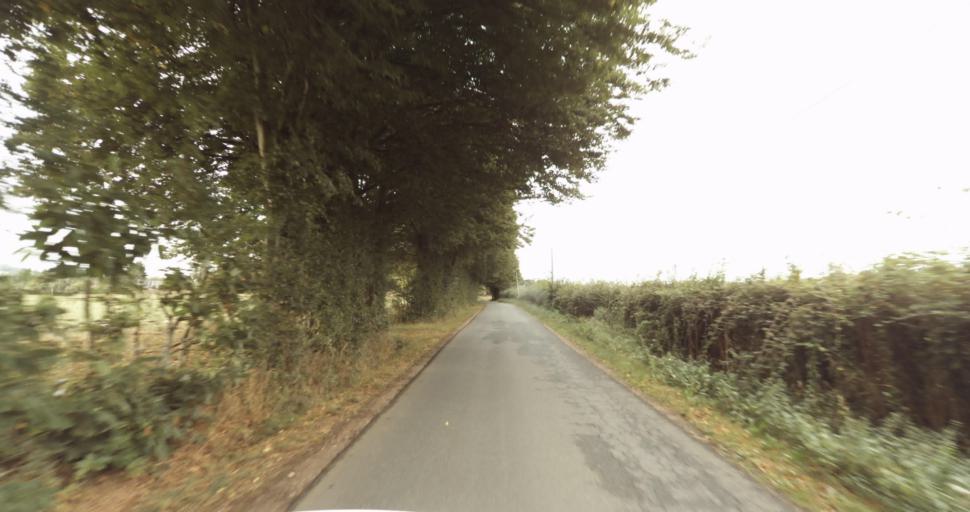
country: FR
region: Lower Normandy
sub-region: Departement du Calvados
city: Livarot
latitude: 48.9407
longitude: 0.1132
